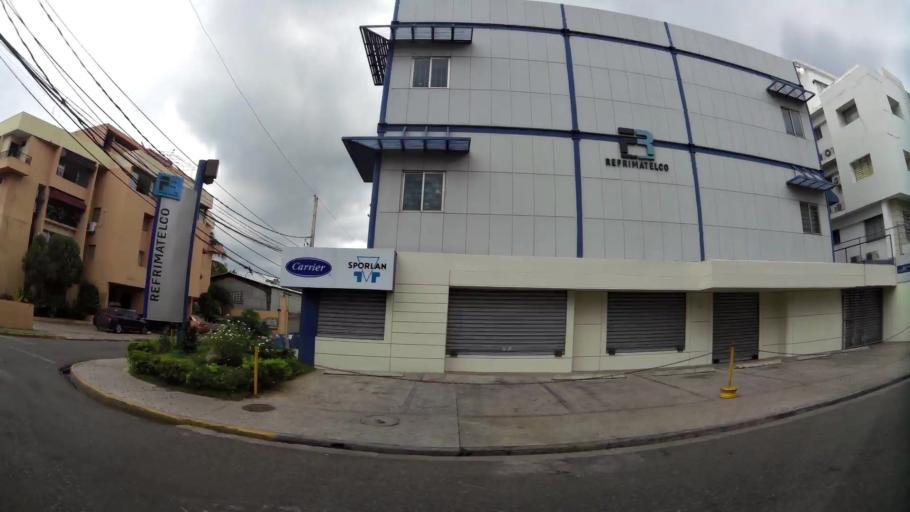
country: DO
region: Nacional
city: La Agustina
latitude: 18.4909
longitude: -69.9348
